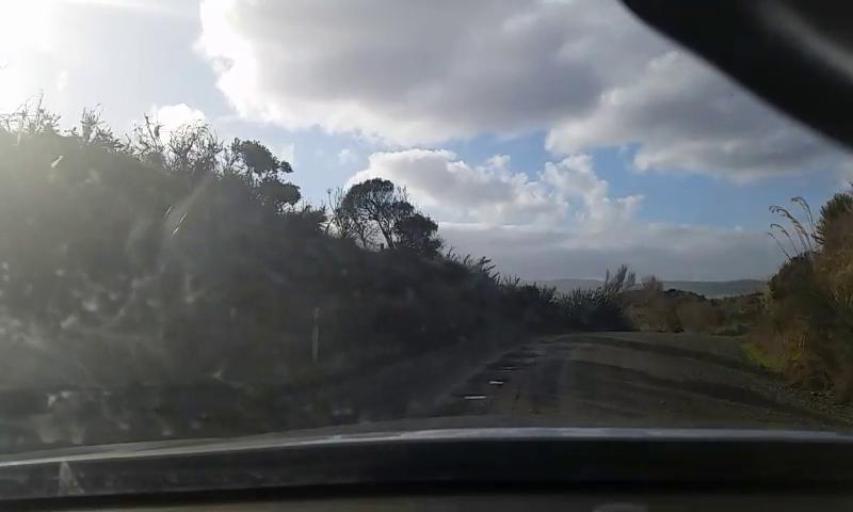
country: NZ
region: Otago
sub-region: Clutha District
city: Papatowai
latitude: -46.6509
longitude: 169.0986
